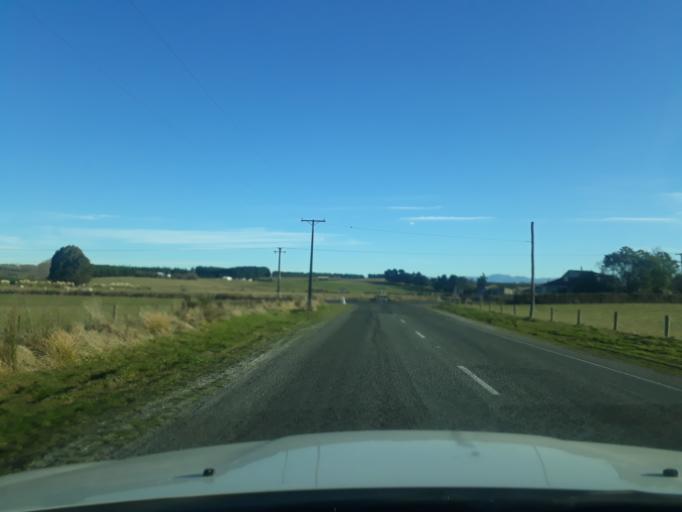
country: NZ
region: Canterbury
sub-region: Timaru District
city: Timaru
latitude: -44.3418
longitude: 171.2010
